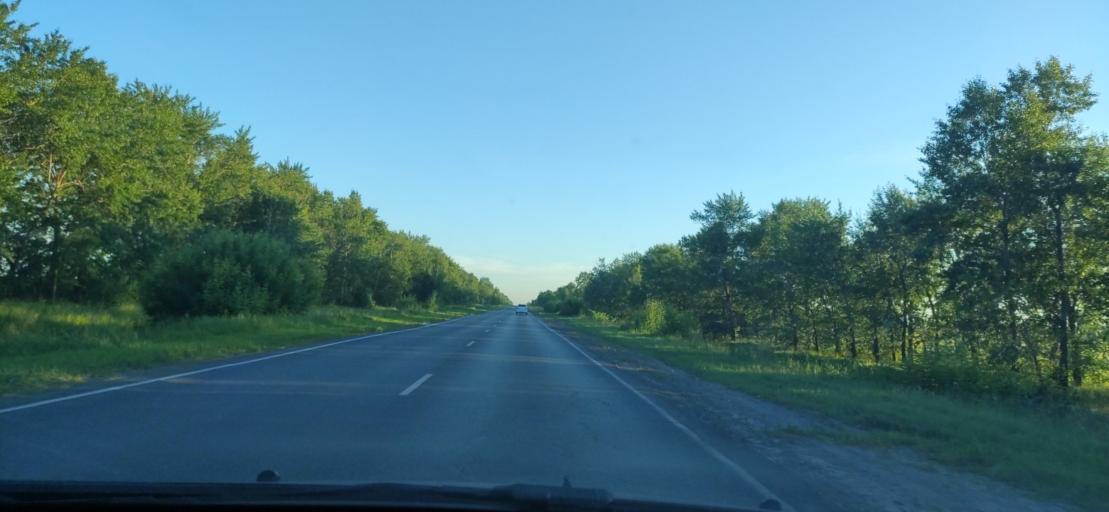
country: RU
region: Ulyanovsk
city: Cherdakly
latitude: 54.4128
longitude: 48.8816
